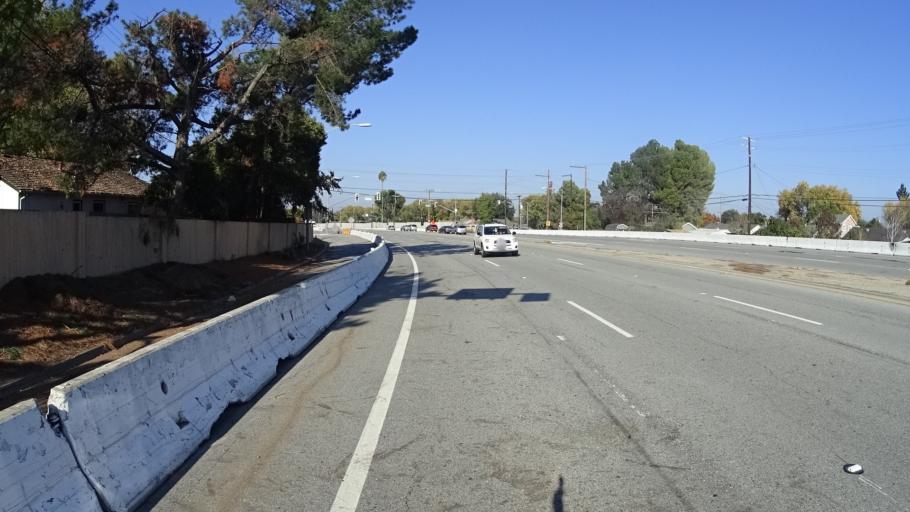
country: US
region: California
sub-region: Santa Clara County
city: Santa Clara
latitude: 37.3453
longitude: -121.9690
